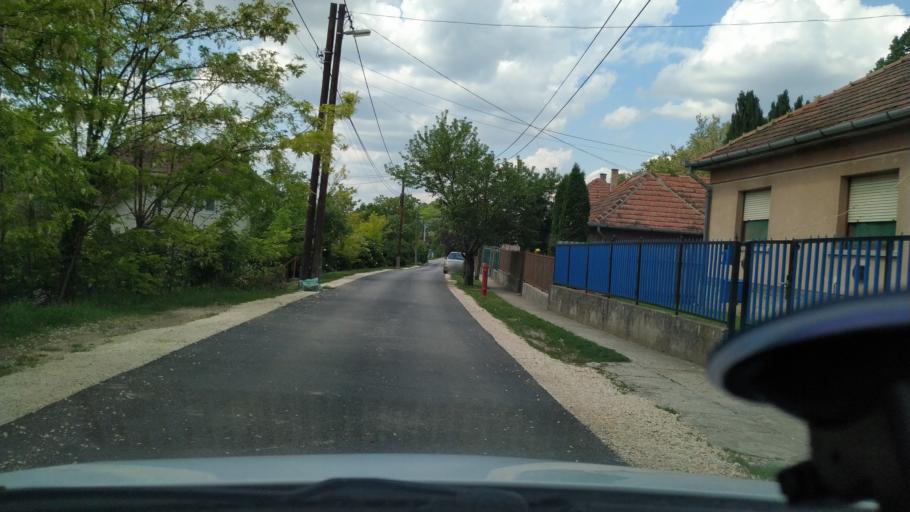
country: HU
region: Pest
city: Mende
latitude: 47.4214
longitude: 19.4508
